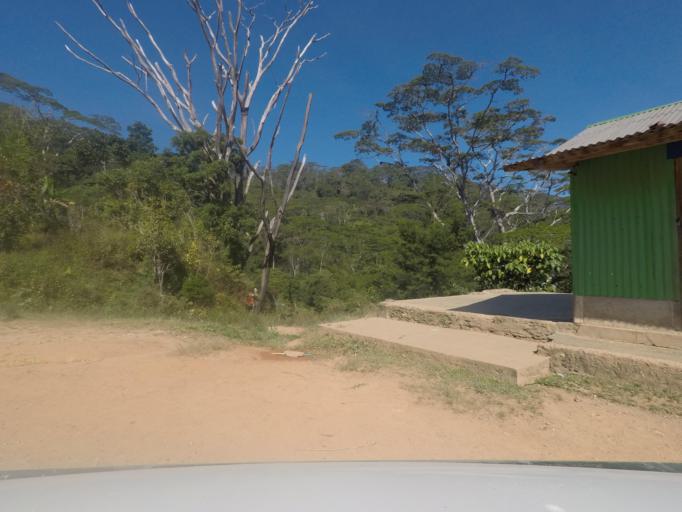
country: TL
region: Ermera
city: Gleno
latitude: -8.7285
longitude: 125.3388
